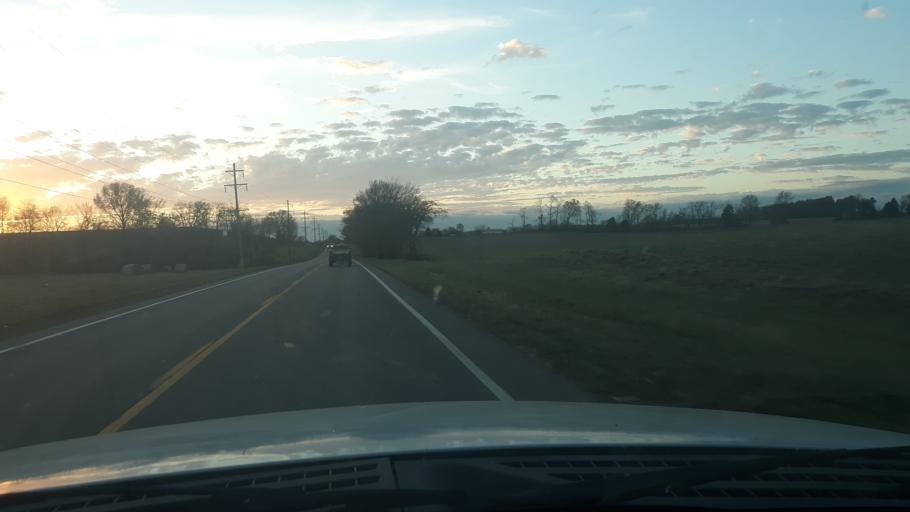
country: US
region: Illinois
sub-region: Saline County
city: Harrisburg
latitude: 37.8347
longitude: -88.5629
